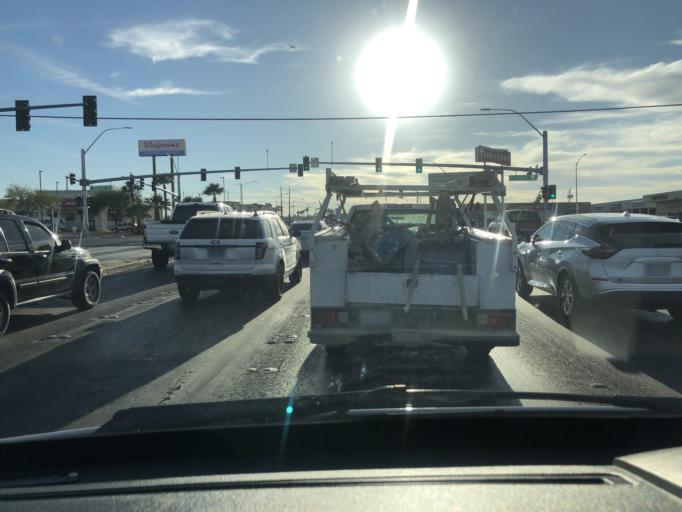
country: US
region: Nevada
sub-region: Clark County
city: Winchester
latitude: 36.1461
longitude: -115.1011
